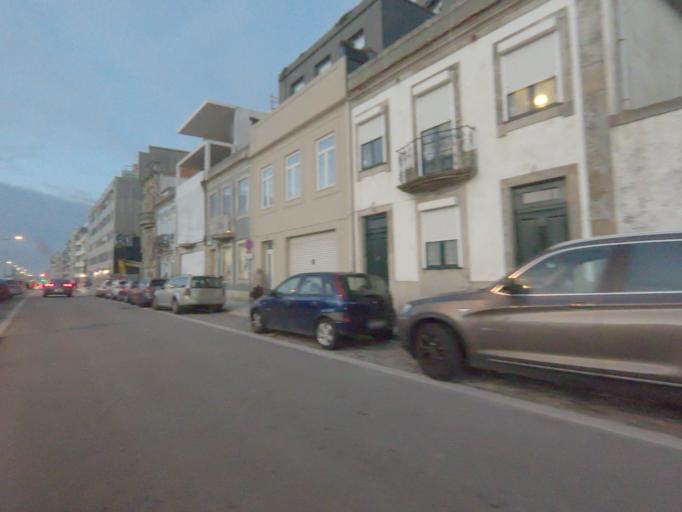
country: PT
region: Porto
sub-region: Matosinhos
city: Matosinhos
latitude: 41.1529
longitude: -8.6782
